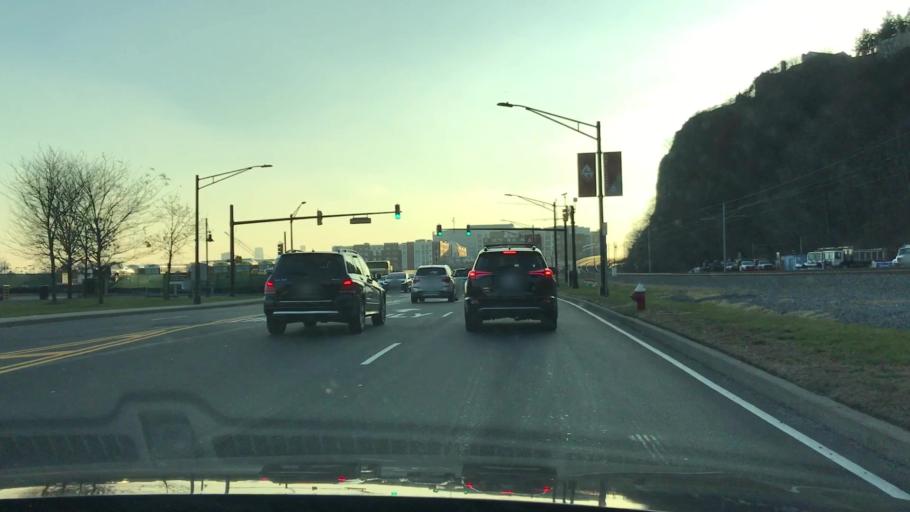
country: US
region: New Jersey
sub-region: Hudson County
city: Weehawken
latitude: 40.7669
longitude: -74.0188
